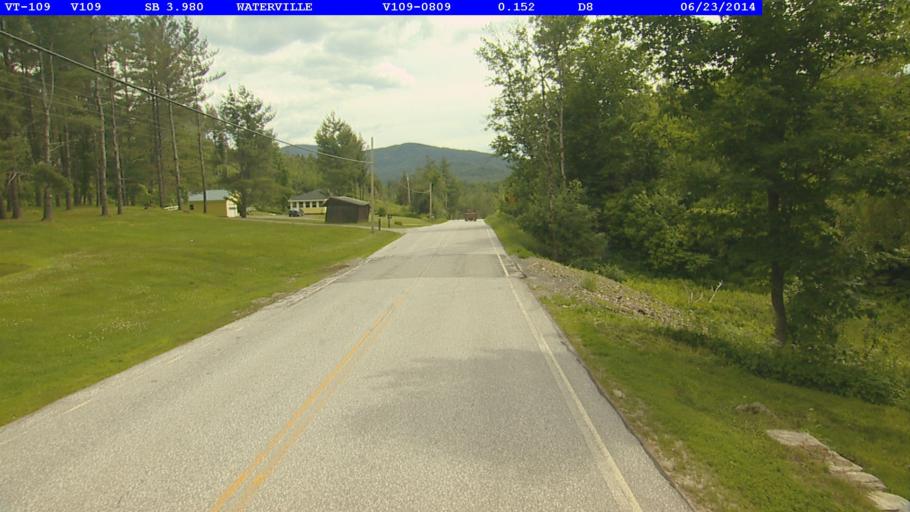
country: US
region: Vermont
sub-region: Lamoille County
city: Johnson
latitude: 44.6848
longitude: -72.7706
